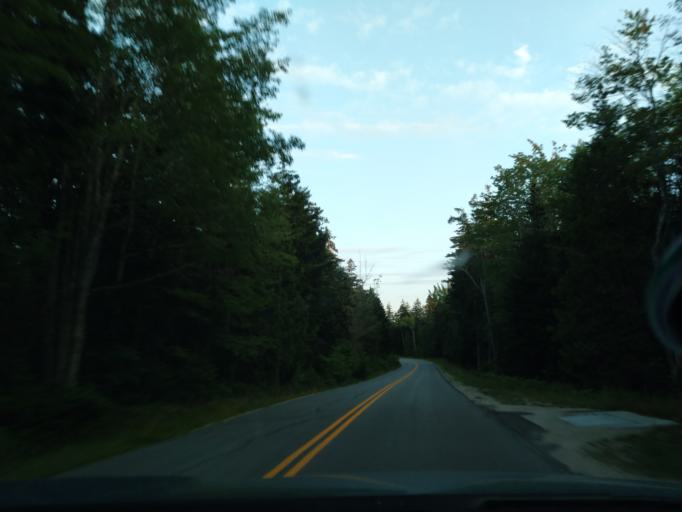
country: US
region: Maine
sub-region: Hancock County
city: Gouldsboro
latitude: 44.3916
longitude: -68.0733
